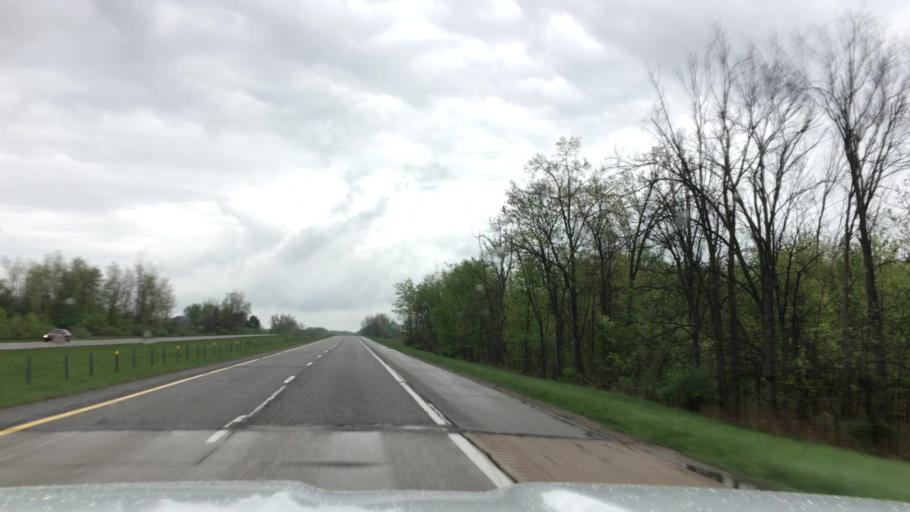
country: US
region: Michigan
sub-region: Shiawassee County
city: Perry
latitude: 42.8448
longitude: -84.1938
